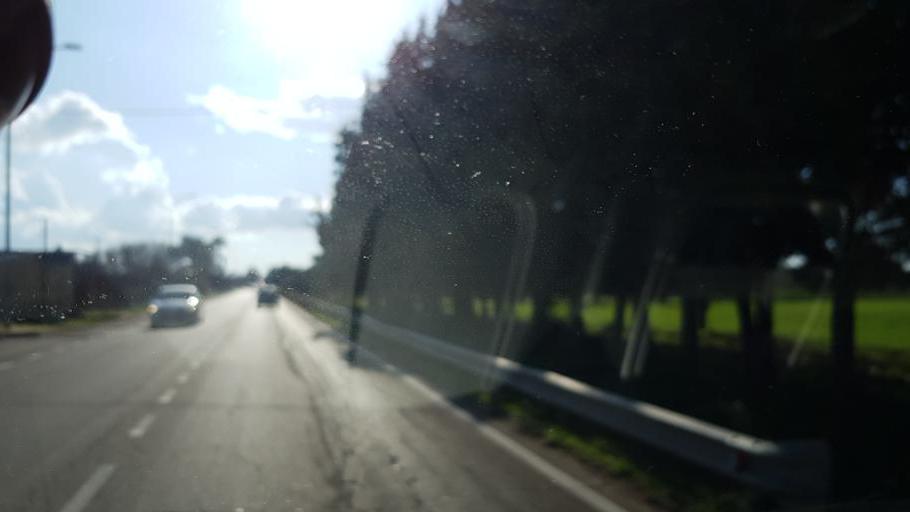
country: IT
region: Apulia
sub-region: Provincia di Lecce
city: Salice Salentino
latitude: 40.3934
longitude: 17.9688
